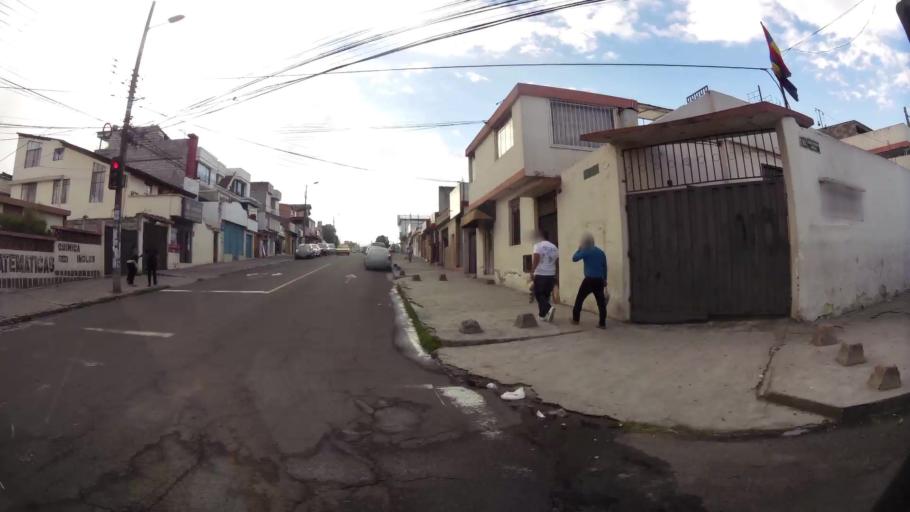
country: EC
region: Pichincha
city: Quito
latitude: -0.1404
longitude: -78.4779
